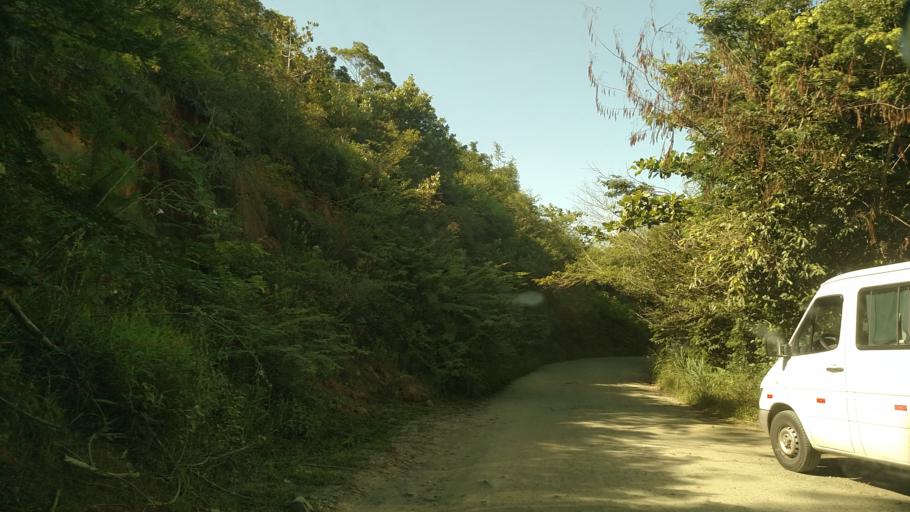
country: BR
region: Santa Catarina
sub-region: Porto Belo
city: Porto Belo
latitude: -27.2130
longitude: -48.5096
